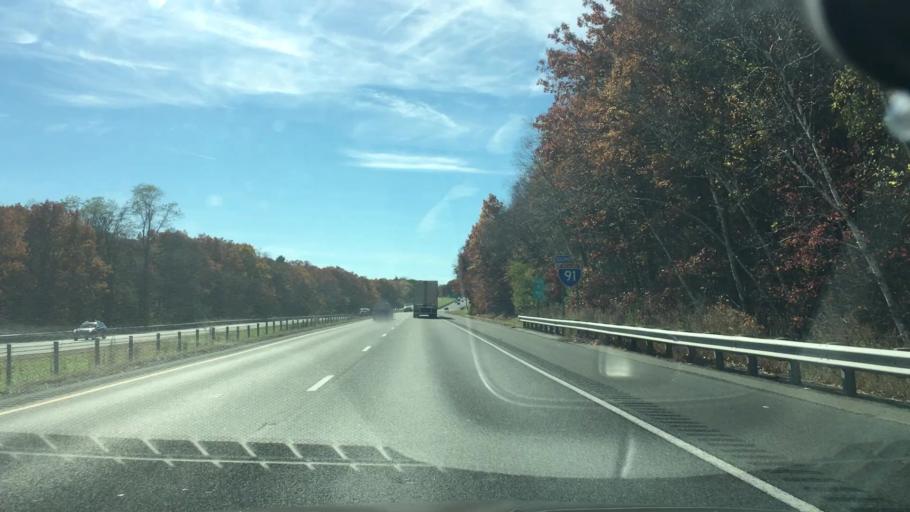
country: US
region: Massachusetts
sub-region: Hampden County
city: Holyoke
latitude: 42.2379
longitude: -72.6316
